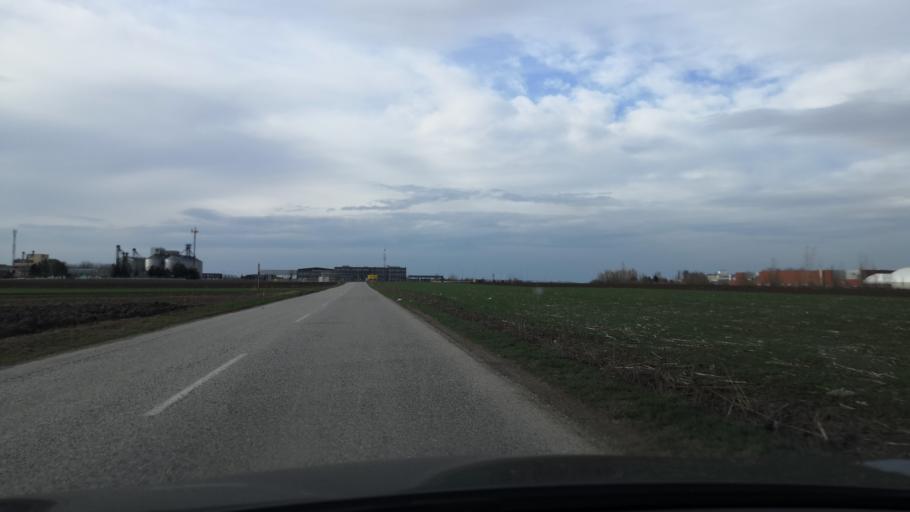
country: RS
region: Autonomna Pokrajina Vojvodina
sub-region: Sremski Okrug
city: Ingija
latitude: 45.0515
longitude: 20.1062
